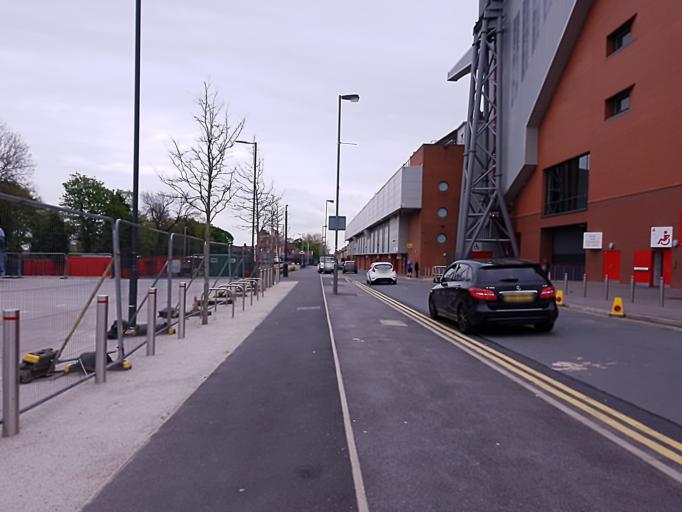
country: GB
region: England
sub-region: Liverpool
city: Liverpool
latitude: 53.4321
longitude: -2.9614
